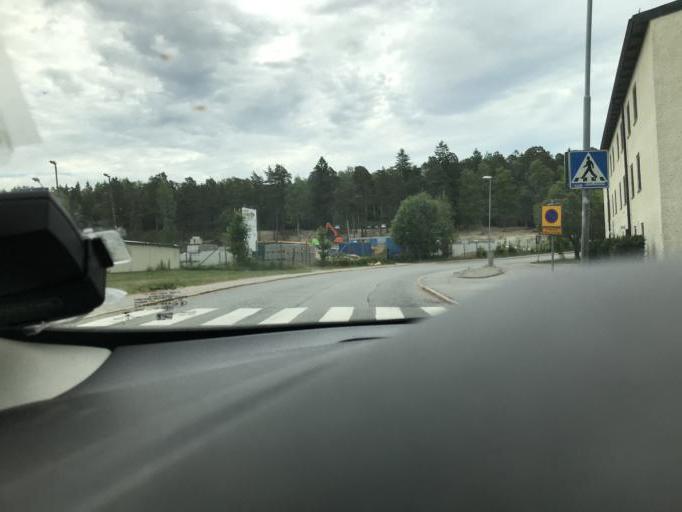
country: SE
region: Stockholm
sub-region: Botkyrka Kommun
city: Tumba
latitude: 59.1972
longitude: 17.8047
